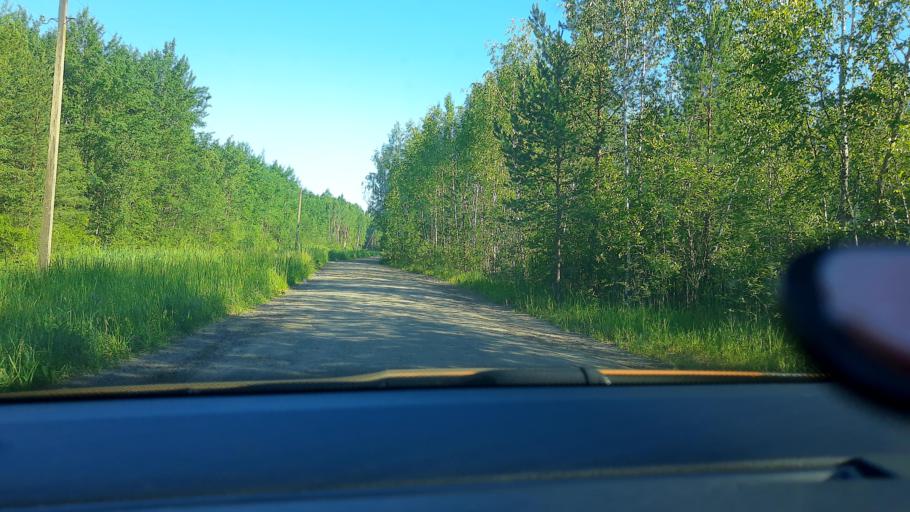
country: RU
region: Moskovskaya
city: Elektrogorsk
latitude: 55.8943
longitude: 38.7176
